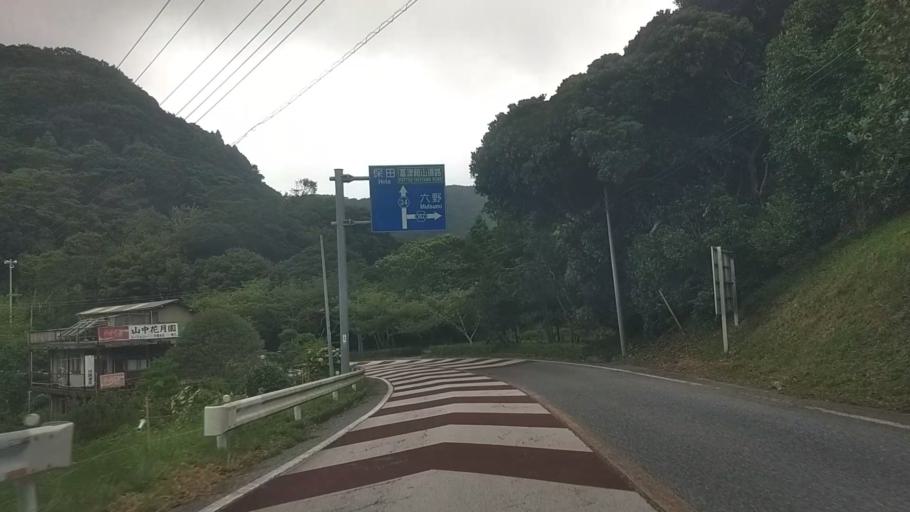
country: JP
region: Chiba
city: Tateyama
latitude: 35.1432
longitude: 139.9166
